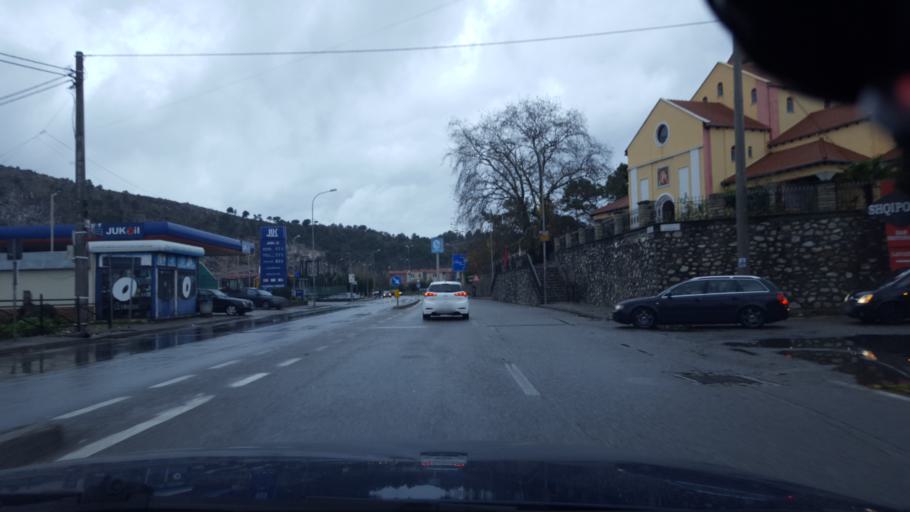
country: AL
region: Shkoder
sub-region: Rrethi i Shkodres
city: Berdica e Madhe
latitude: 42.0436
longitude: 19.4910
